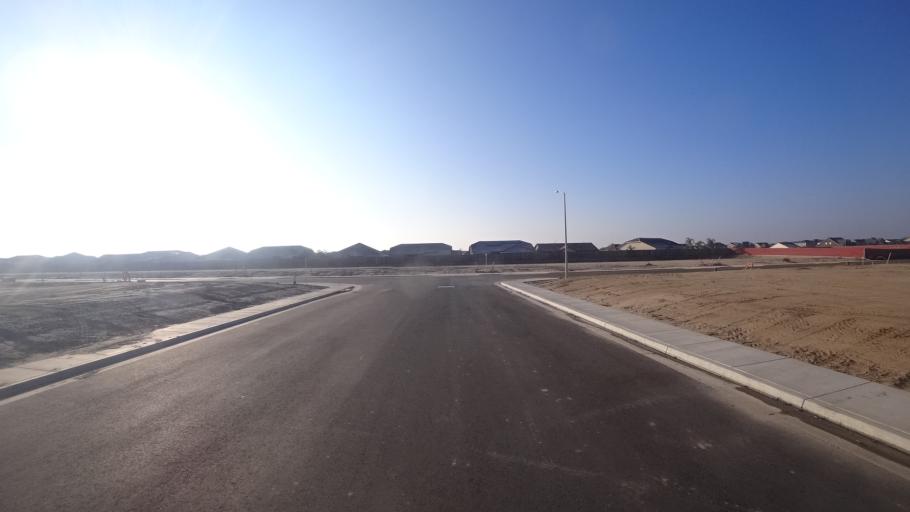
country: US
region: California
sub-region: Kern County
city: Greenacres
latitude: 35.2933
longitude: -119.1125
